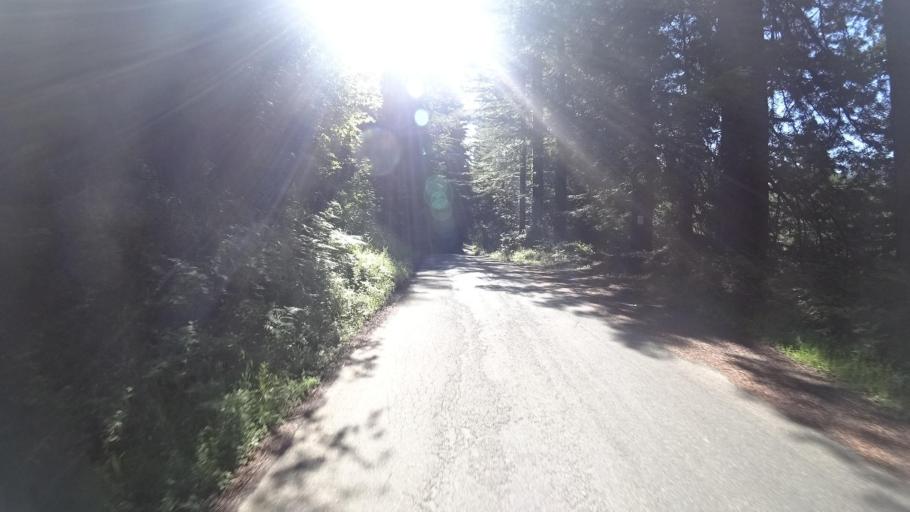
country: US
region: California
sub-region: Humboldt County
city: Rio Dell
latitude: 40.4605
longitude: -124.0434
